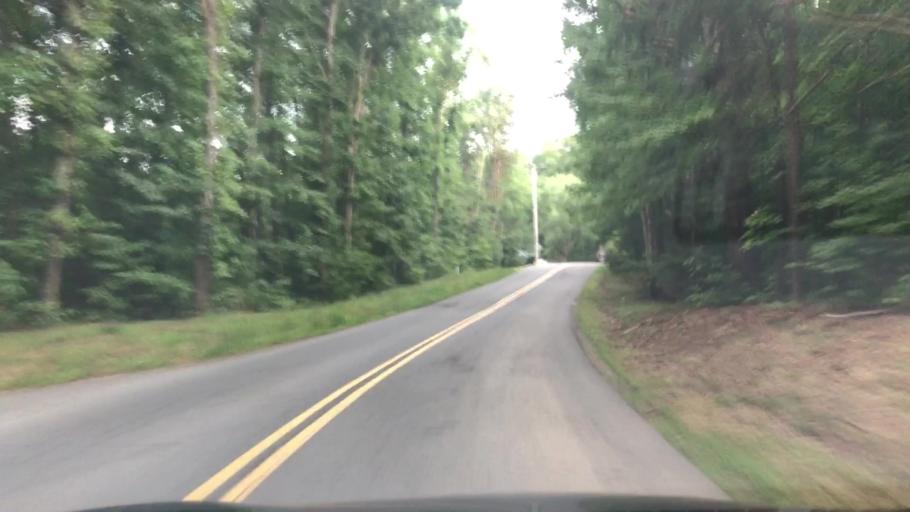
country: US
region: Virginia
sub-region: Fauquier County
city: Bealeton
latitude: 38.5190
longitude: -77.6817
